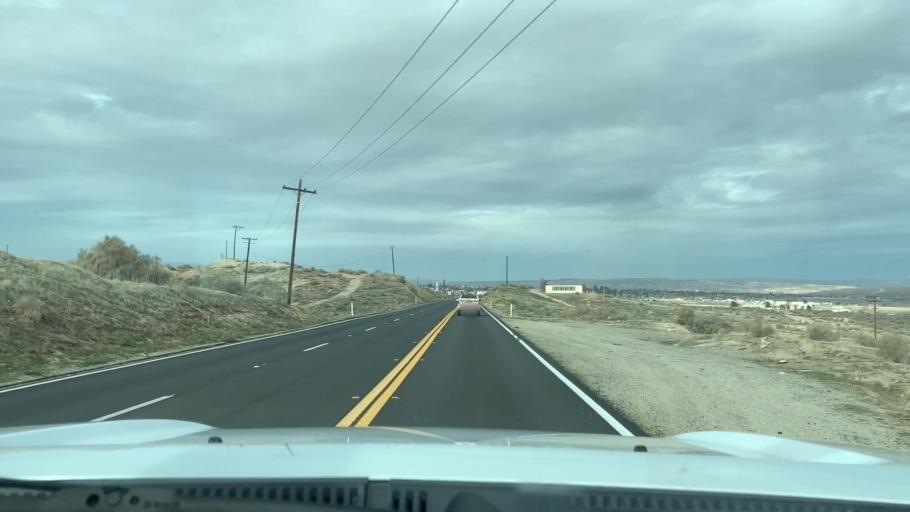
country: US
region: California
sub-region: Kern County
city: South Taft
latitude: 35.1225
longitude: -119.4367
